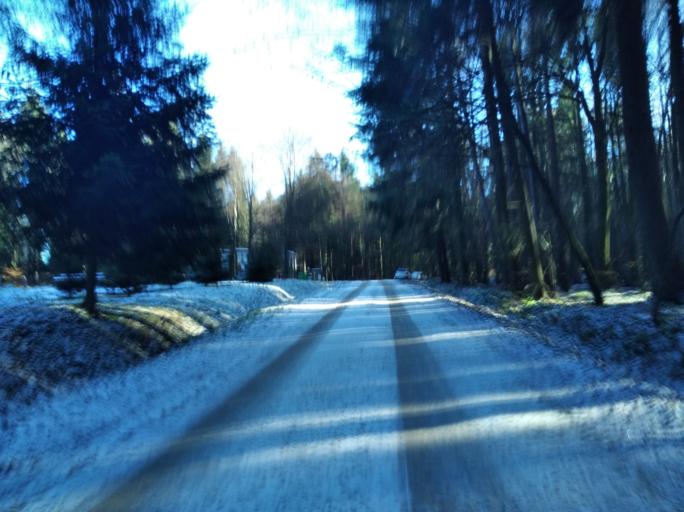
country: PL
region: Subcarpathian Voivodeship
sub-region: Powiat ropczycko-sedziszowski
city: Iwierzyce
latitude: 49.9719
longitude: 21.7720
